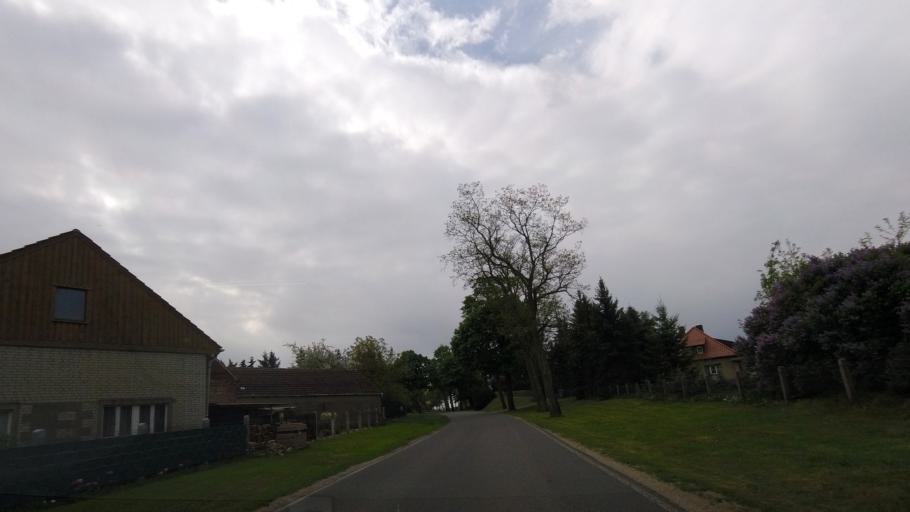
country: DE
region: Brandenburg
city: Dahme
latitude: 51.8950
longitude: 13.4114
